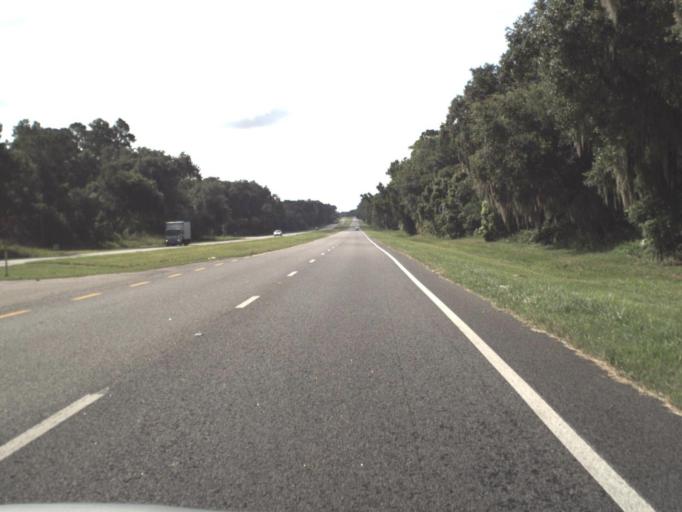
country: US
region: Florida
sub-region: Alachua County
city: Gainesville
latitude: 29.5002
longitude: -82.2629
